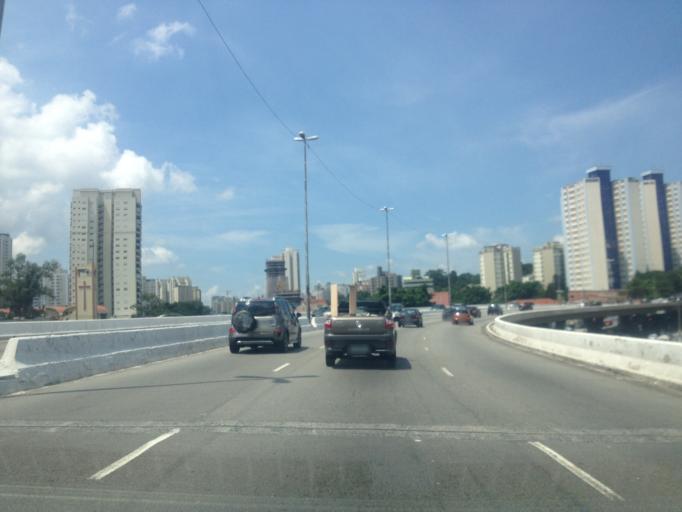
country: BR
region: Sao Paulo
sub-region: Diadema
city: Diadema
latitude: -23.6430
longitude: -46.6725
